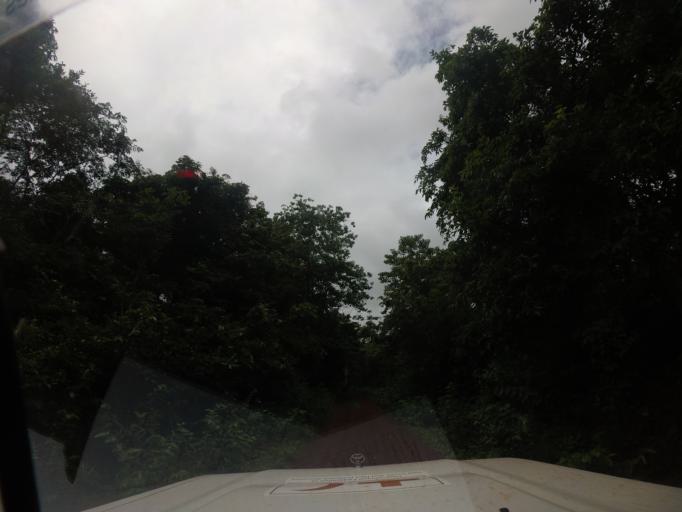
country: SL
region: Northern Province
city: Kamakwie
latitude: 9.6904
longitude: -12.2664
